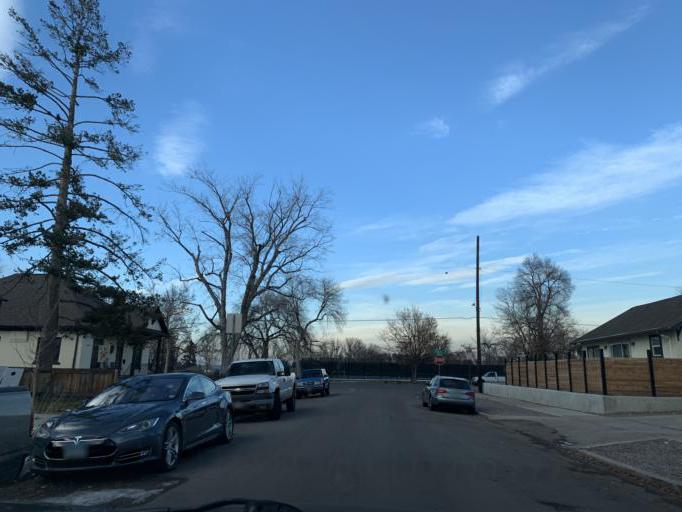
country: US
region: Colorado
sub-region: Adams County
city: Berkley
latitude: 39.7797
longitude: -105.0463
